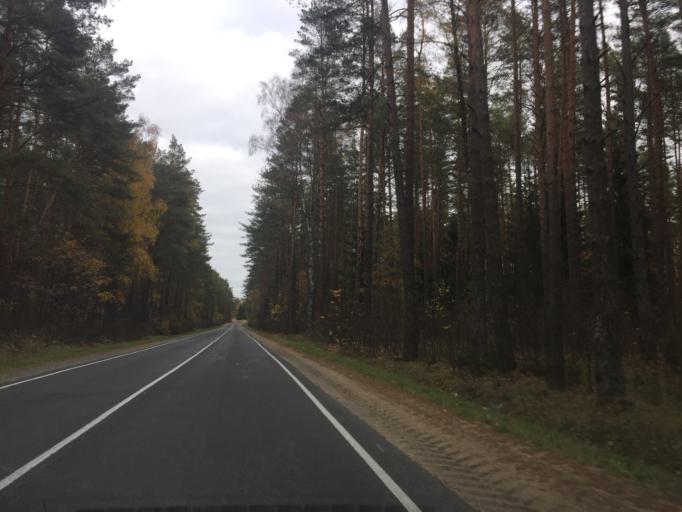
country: BY
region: Minsk
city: Svir
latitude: 54.8195
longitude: 26.1814
